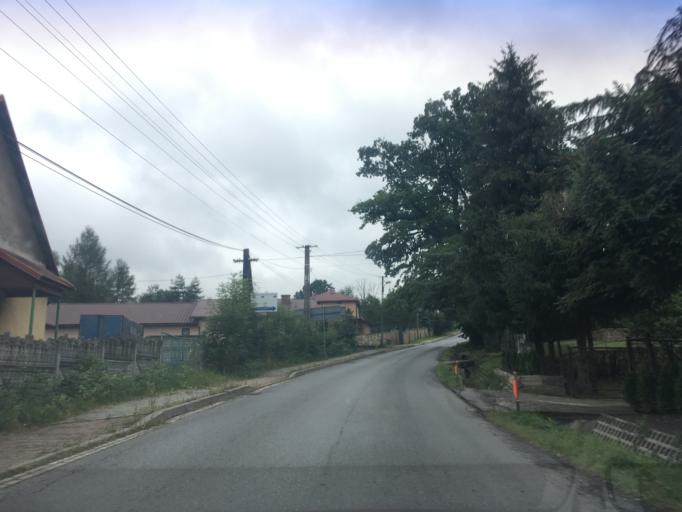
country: PL
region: Lesser Poland Voivodeship
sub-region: Powiat myslenicki
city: Wisniowa
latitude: 49.7874
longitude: 20.1145
